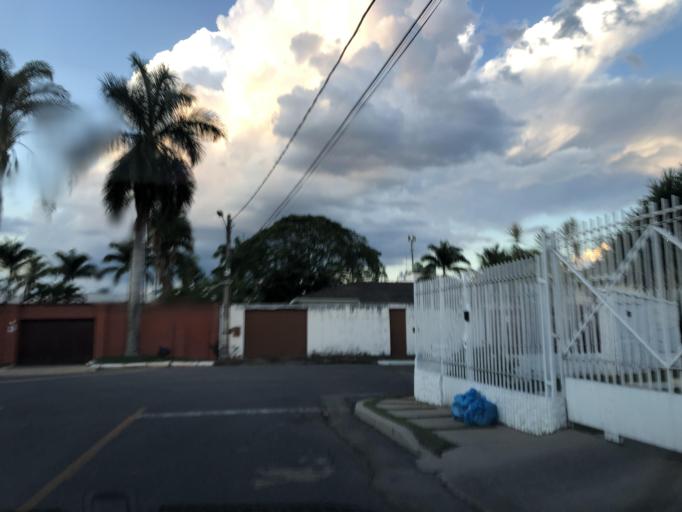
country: BR
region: Federal District
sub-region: Brasilia
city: Brasilia
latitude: -15.8474
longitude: -47.8944
